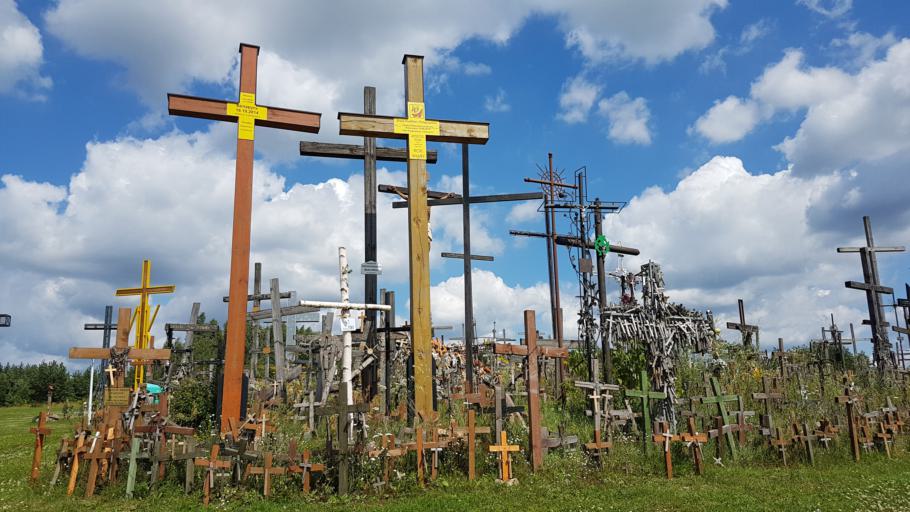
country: PL
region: Podlasie
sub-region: Powiat bialostocki
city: Wasilkow
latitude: 53.2217
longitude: 23.2214
